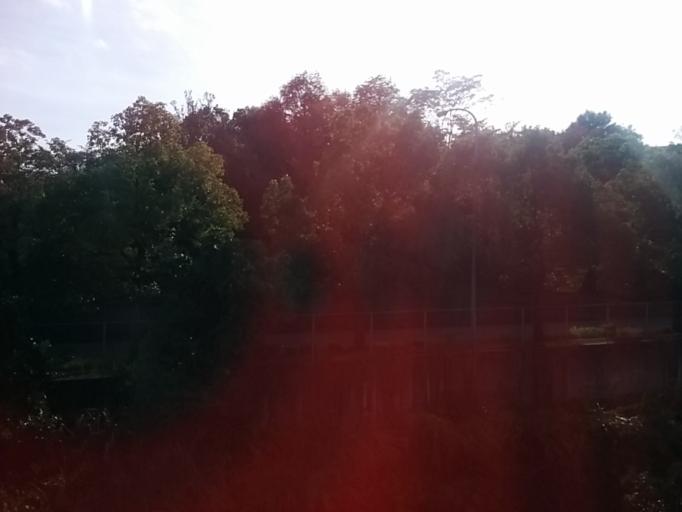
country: JP
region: Nara
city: Nara-shi
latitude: 34.7258
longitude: 135.7920
